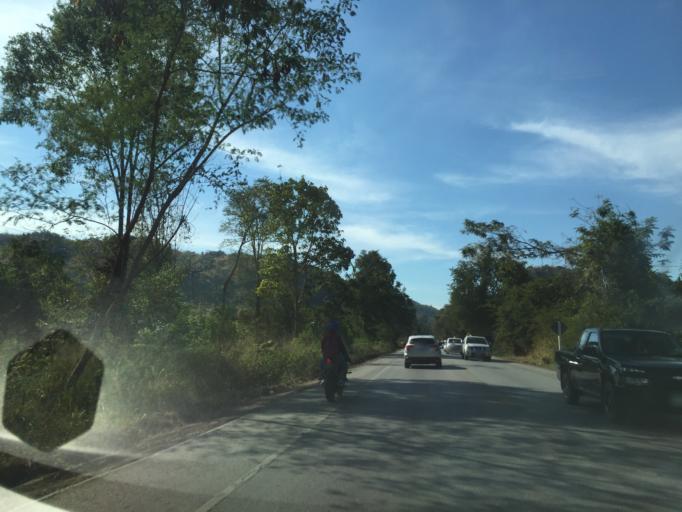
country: TH
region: Loei
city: Wang Saphung
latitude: 17.2882
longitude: 101.8372
